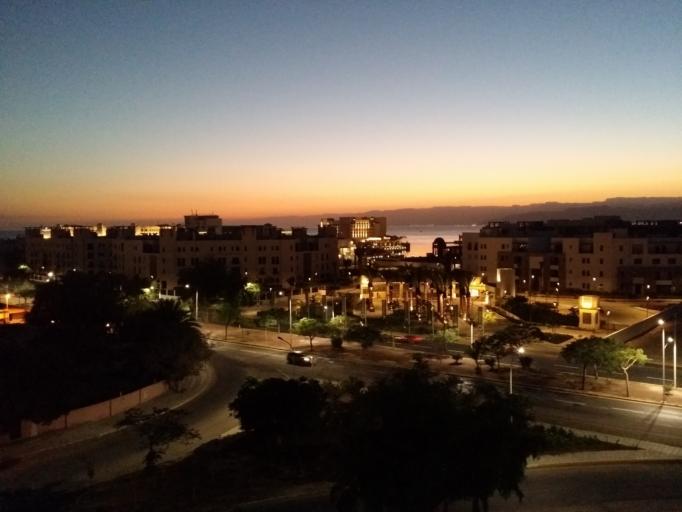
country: JO
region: Aqaba
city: Aqaba
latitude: 29.5402
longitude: 34.9992
